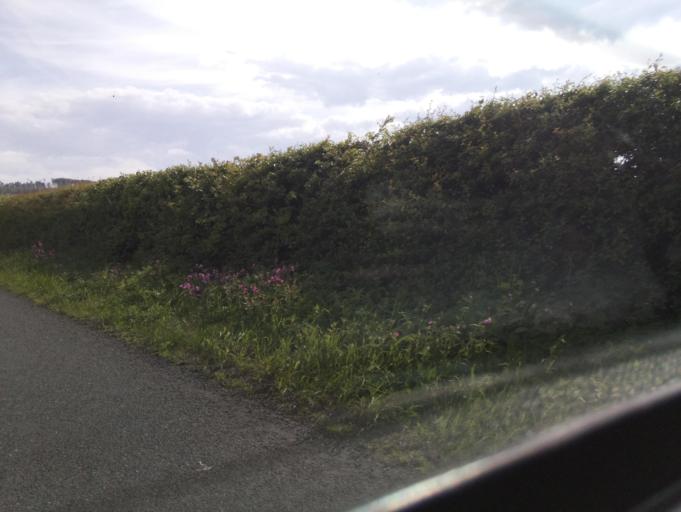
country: GB
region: England
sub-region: Northumberland
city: Ellingham
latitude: 55.4646
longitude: -1.7187
